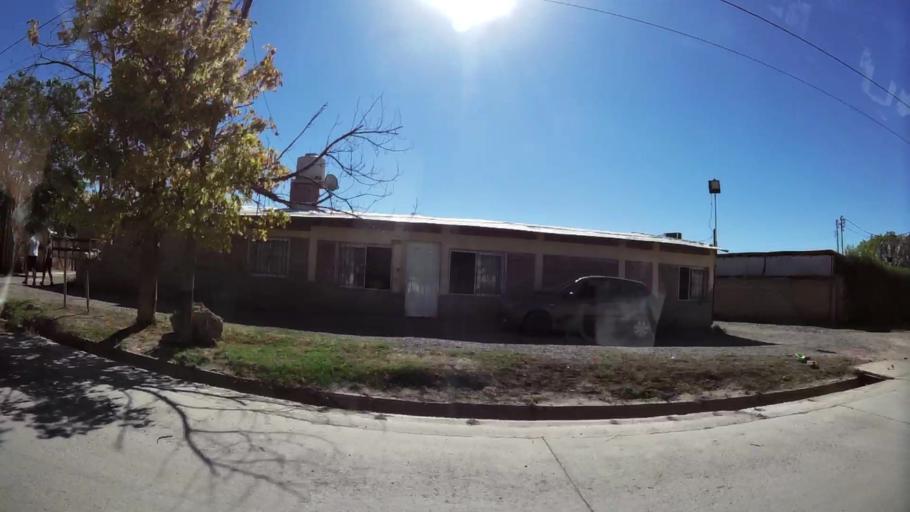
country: AR
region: Mendoza
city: Las Heras
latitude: -32.8357
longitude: -68.8161
